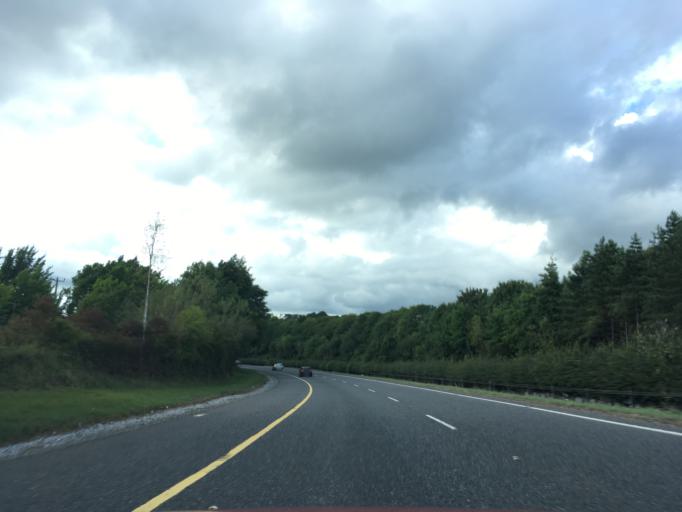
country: IE
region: Munster
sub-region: County Cork
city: Passage West
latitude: 51.9309
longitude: -8.3745
